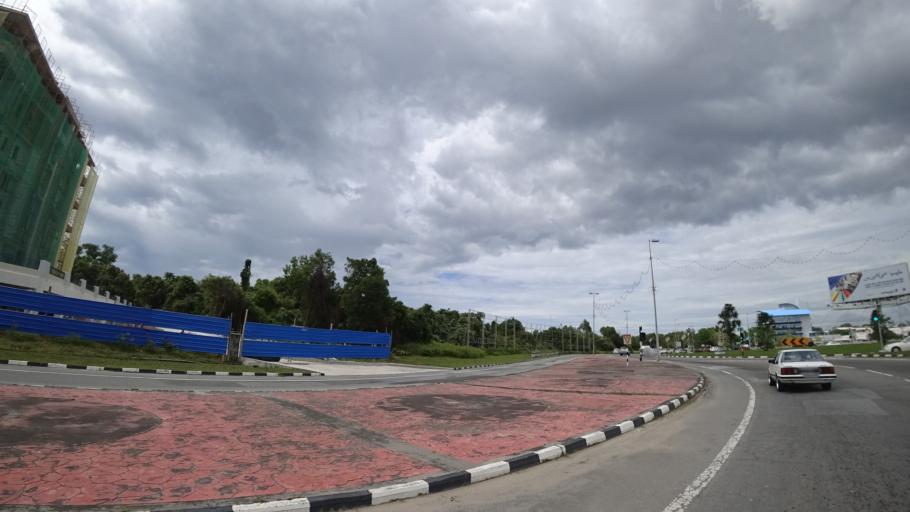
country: BN
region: Brunei and Muara
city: Bandar Seri Begawan
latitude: 4.8950
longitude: 114.8999
